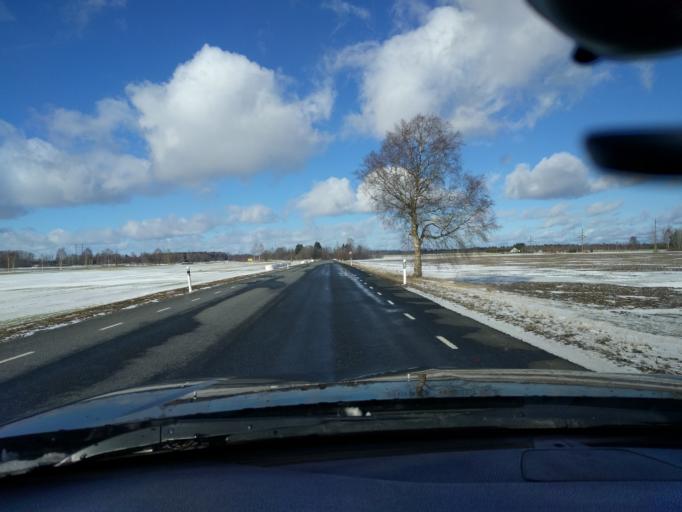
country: EE
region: Harju
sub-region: Anija vald
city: Kehra
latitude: 59.2489
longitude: 25.3459
